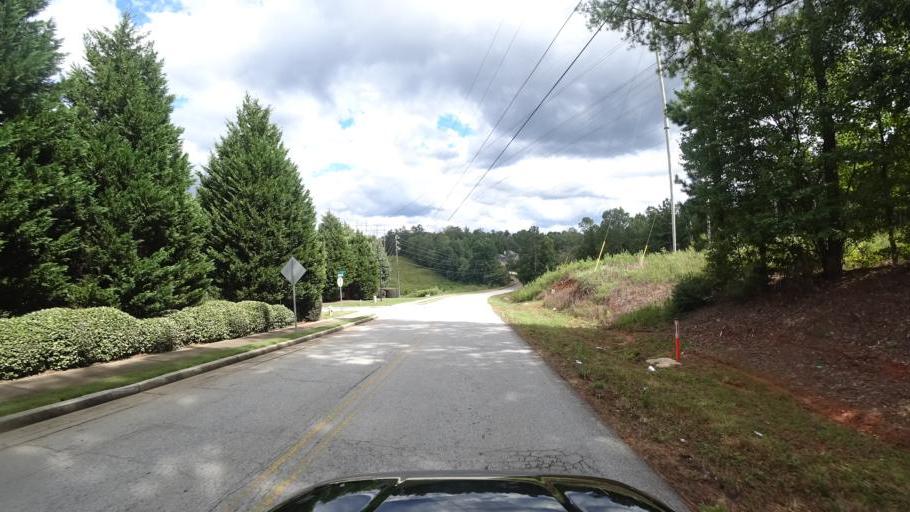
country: US
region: Georgia
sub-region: DeKalb County
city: Panthersville
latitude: 33.6491
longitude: -84.2225
